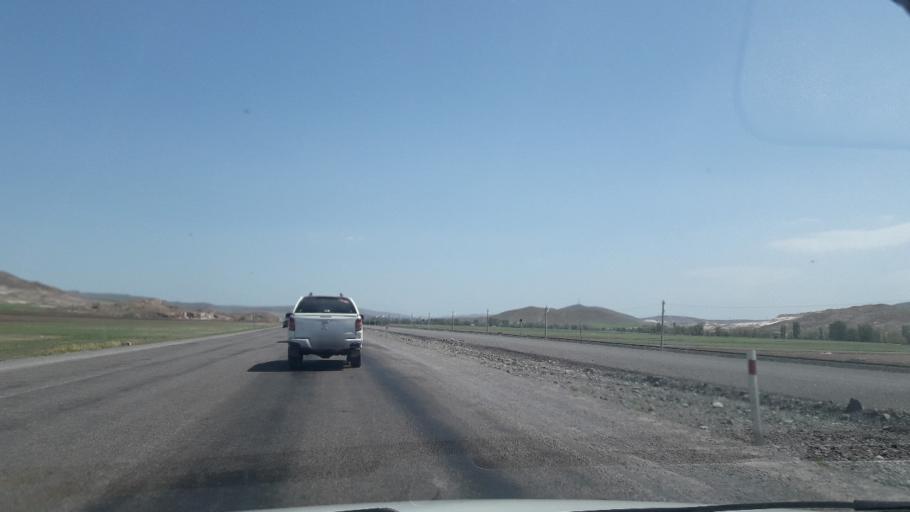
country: TR
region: Sivas
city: Ulas
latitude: 39.5291
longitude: 37.0142
